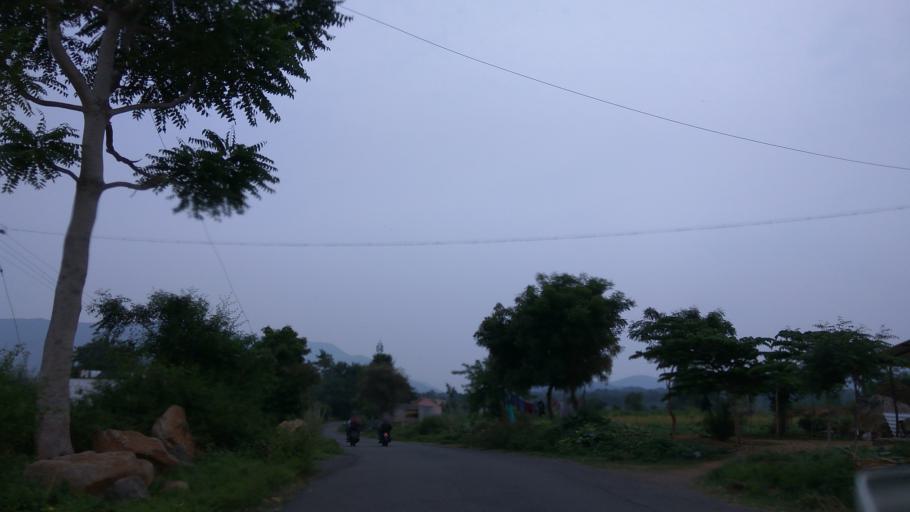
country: IN
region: Tamil Nadu
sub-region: Dharmapuri
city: Dharmapuri
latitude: 12.0228
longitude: 78.1136
